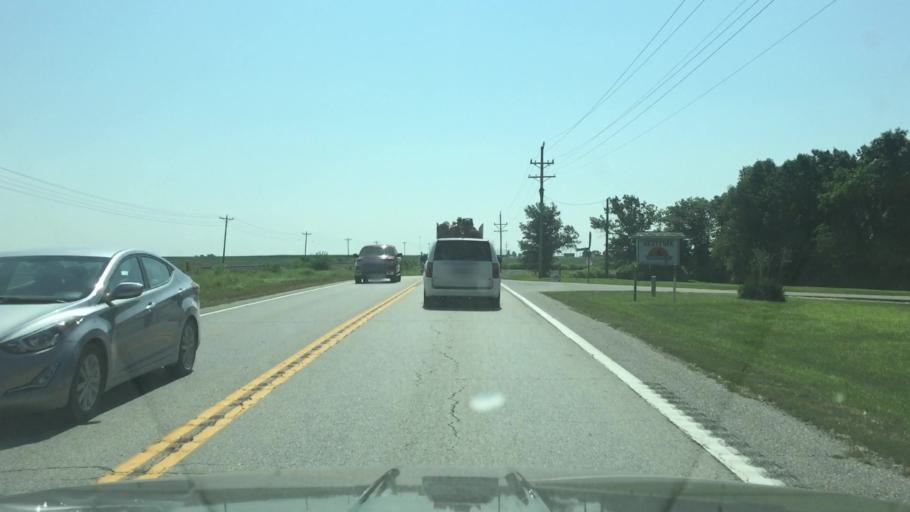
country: US
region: Missouri
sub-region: Moniteau County
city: Tipton
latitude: 38.6712
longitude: -92.8513
